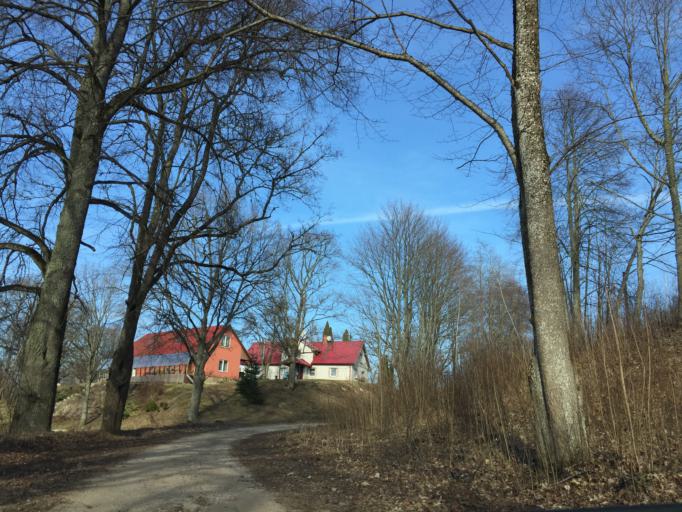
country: LV
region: Krimulda
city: Ragana
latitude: 57.3282
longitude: 24.6395
